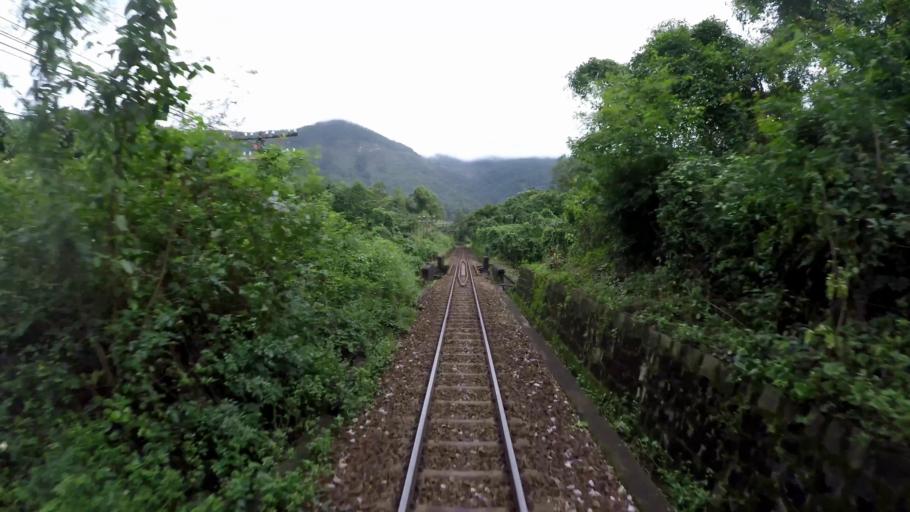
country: VN
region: Da Nang
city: Lien Chieu
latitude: 16.2081
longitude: 108.1194
